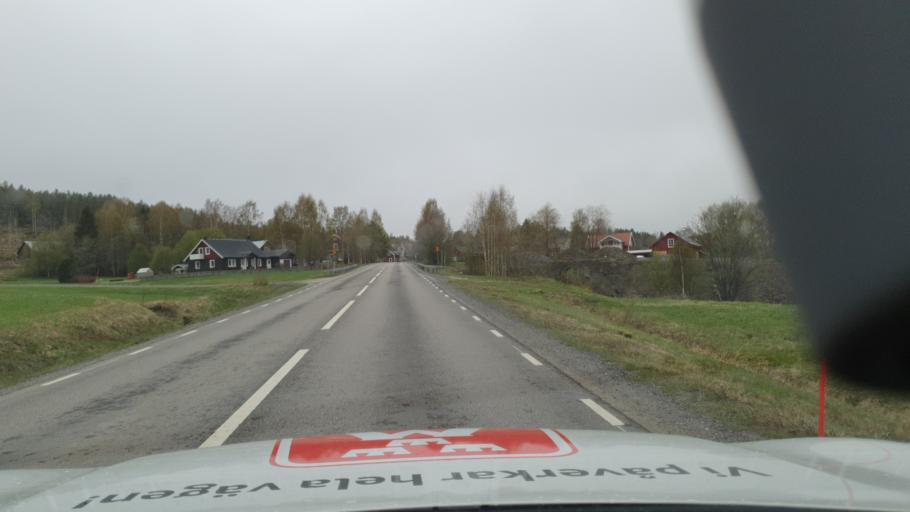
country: SE
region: Vaesterbotten
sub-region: Vannas Kommun
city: Vannasby
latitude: 63.7800
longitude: 19.8446
